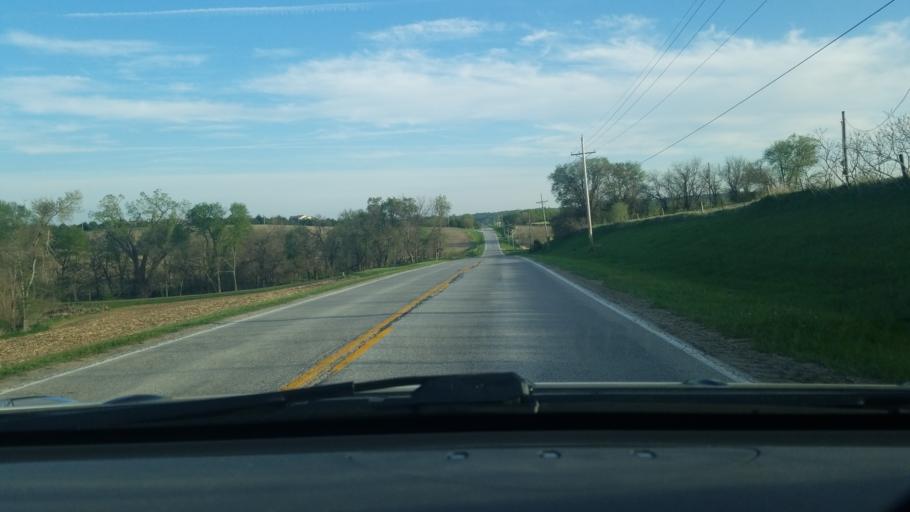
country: US
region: Nebraska
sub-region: Sarpy County
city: Offutt Air Force Base
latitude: 41.0834
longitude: -95.9665
